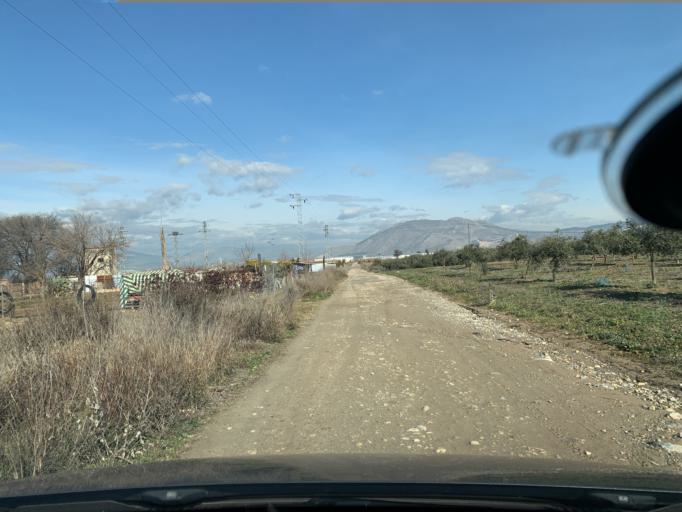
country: ES
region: Andalusia
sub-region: Provincia de Granada
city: Chauchina
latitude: 37.1806
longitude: -3.7506
